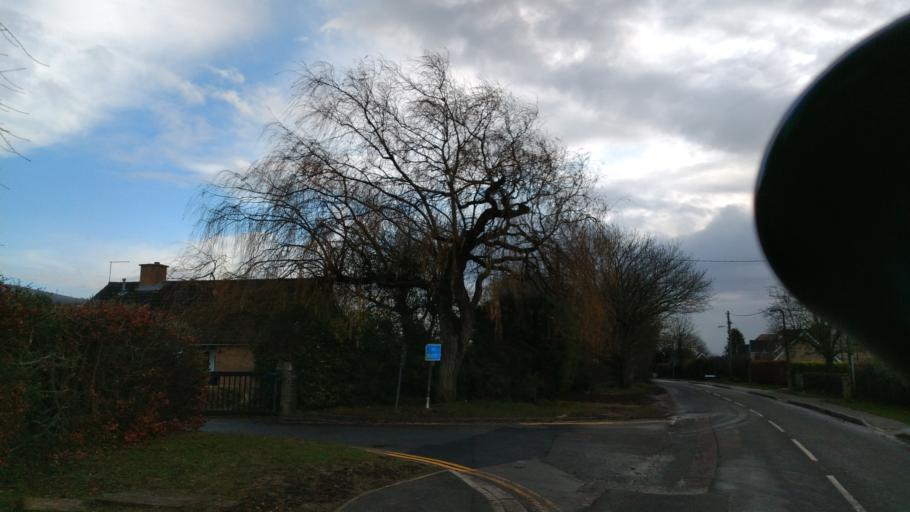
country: GB
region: England
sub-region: Borough of Swindon
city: Highworth
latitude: 51.6262
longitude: -1.7100
